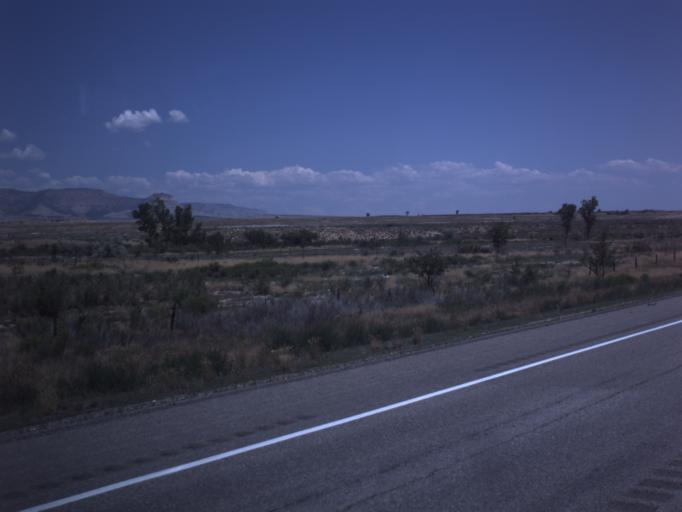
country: US
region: Utah
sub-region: Emery County
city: Orangeville
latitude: 39.1570
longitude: -111.0777
